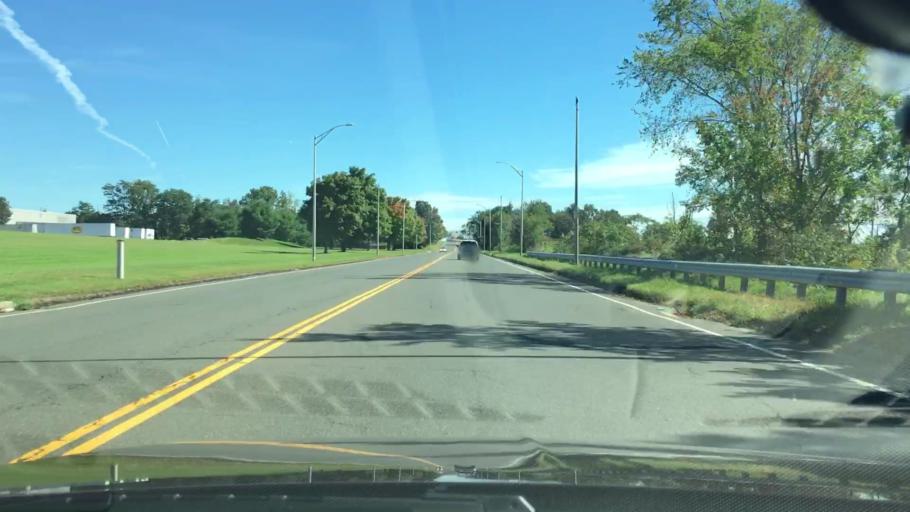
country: US
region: Connecticut
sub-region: Litchfield County
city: Terryville
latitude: 41.6922
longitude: -72.9807
